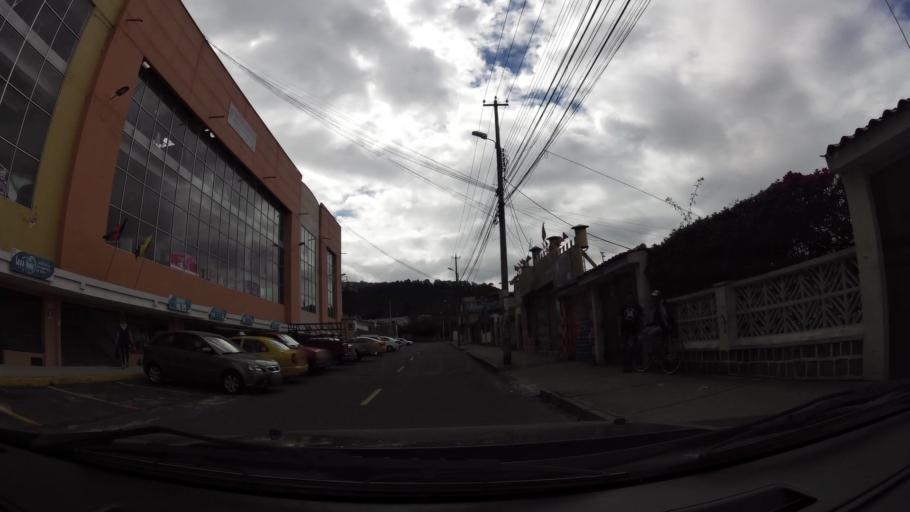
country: EC
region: Pichincha
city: Quito
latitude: -0.1398
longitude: -78.5002
